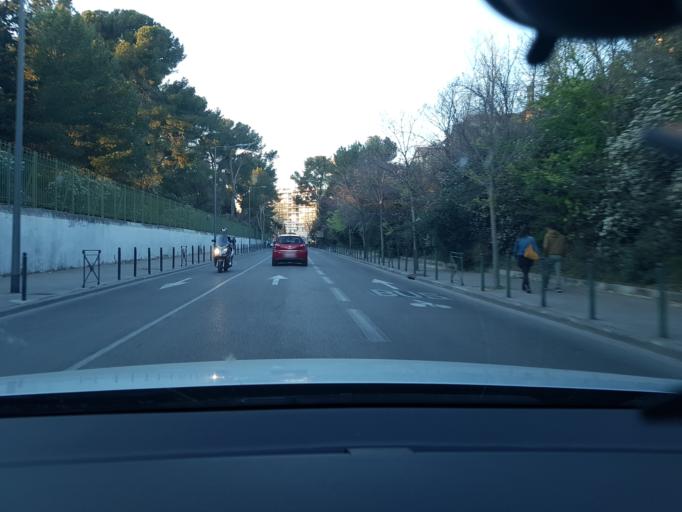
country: FR
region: Provence-Alpes-Cote d'Azur
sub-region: Departement des Bouches-du-Rhone
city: Aix-en-Provence
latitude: 43.5213
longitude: 5.4426
